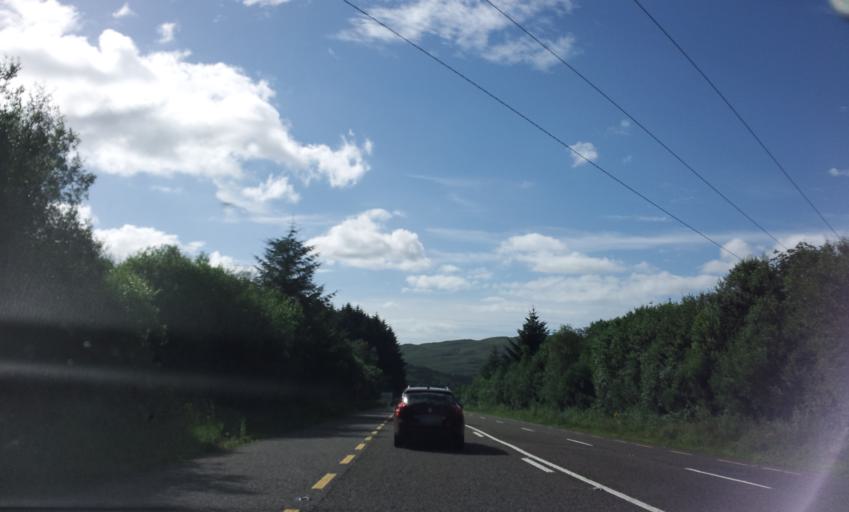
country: IE
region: Munster
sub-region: County Cork
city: Millstreet
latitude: 51.9809
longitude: -9.2619
